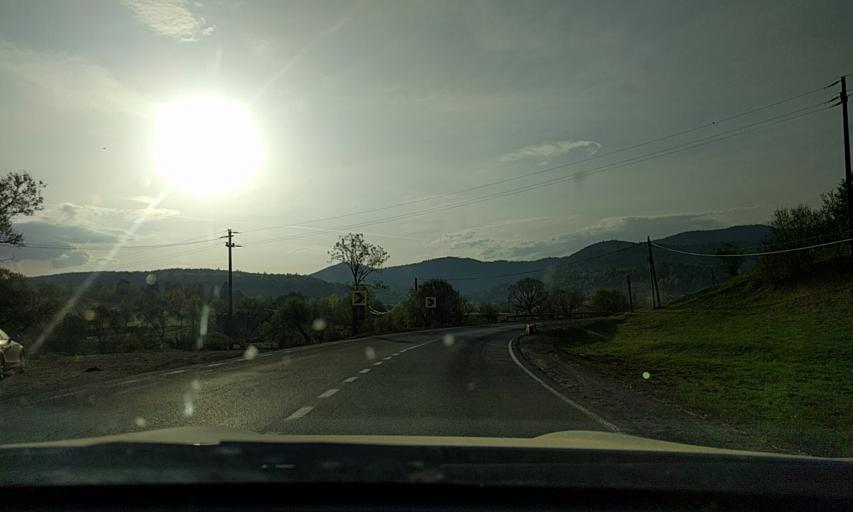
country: RO
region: Covasna
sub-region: Comuna Bretcu
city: Bretcu
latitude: 46.0476
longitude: 26.3196
